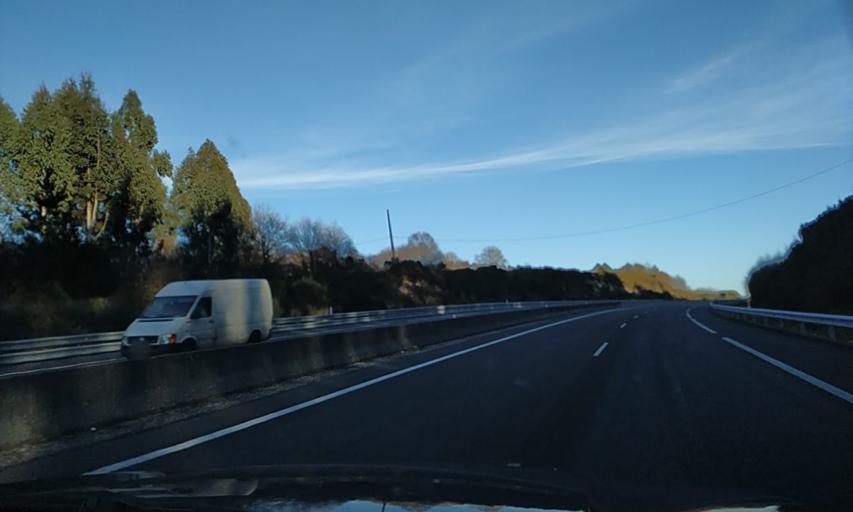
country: ES
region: Galicia
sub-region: Provincia de Pontevedra
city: Dozon
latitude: 42.5620
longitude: -8.0342
